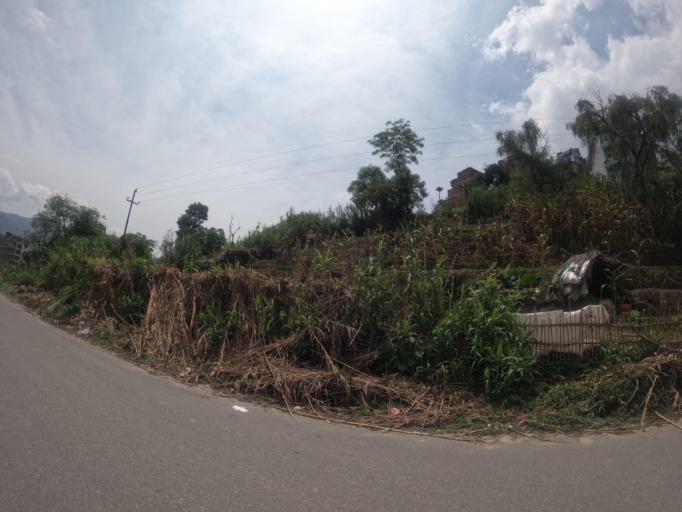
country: NP
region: Central Region
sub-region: Bagmati Zone
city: Bhaktapur
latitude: 27.6786
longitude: 85.3883
